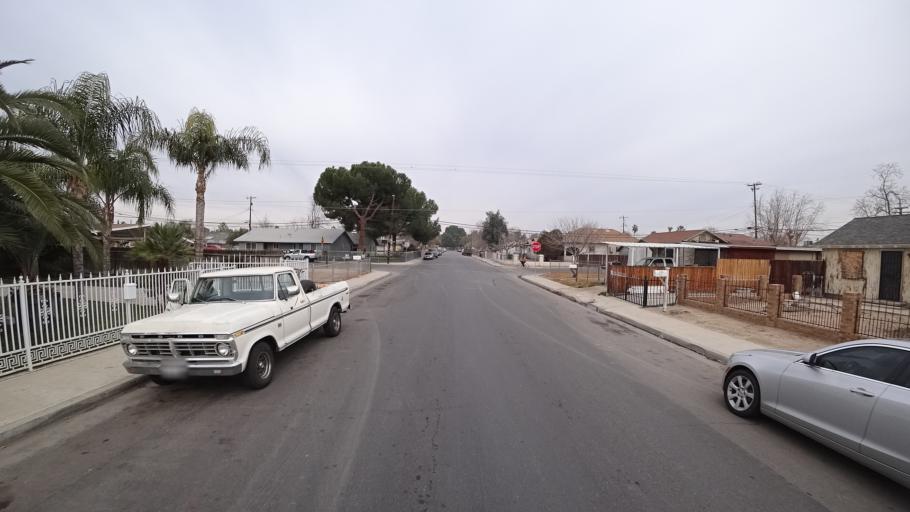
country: US
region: California
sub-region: Kern County
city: Bakersfield
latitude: 35.3590
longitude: -118.9930
